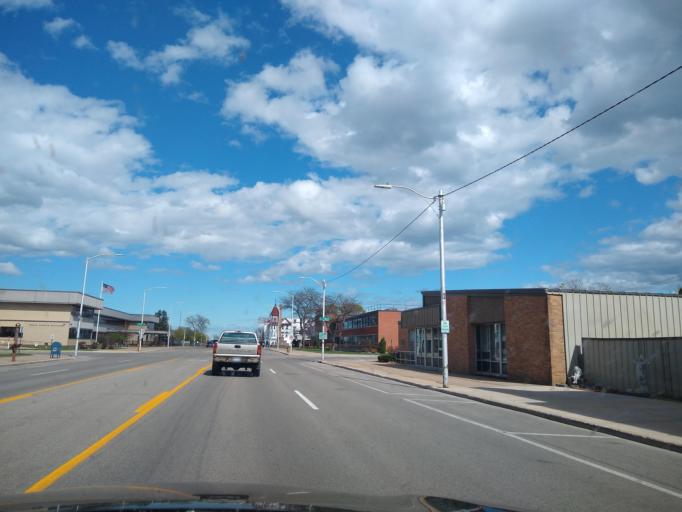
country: US
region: Michigan
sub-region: Delta County
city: Escanaba
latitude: 45.7457
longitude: -87.0531
